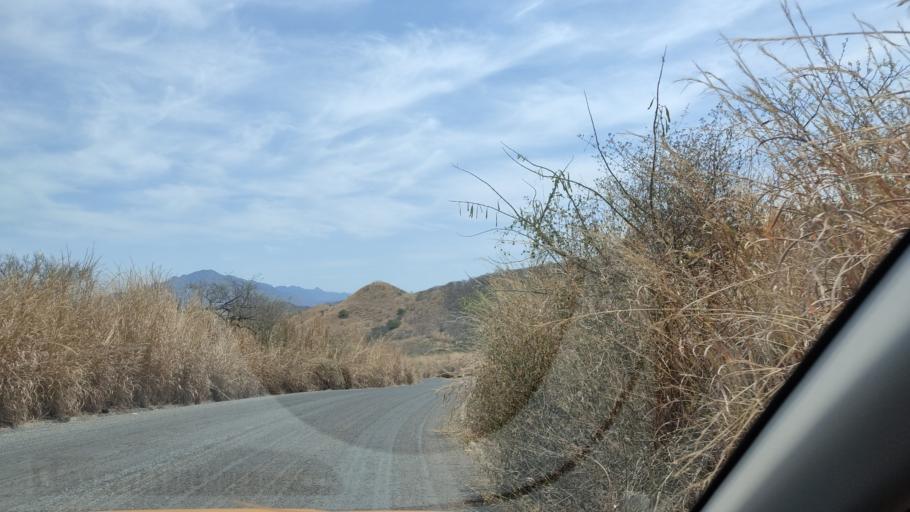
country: MX
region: Nayarit
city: Santa Maria del Oro
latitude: 21.5081
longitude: -104.6062
